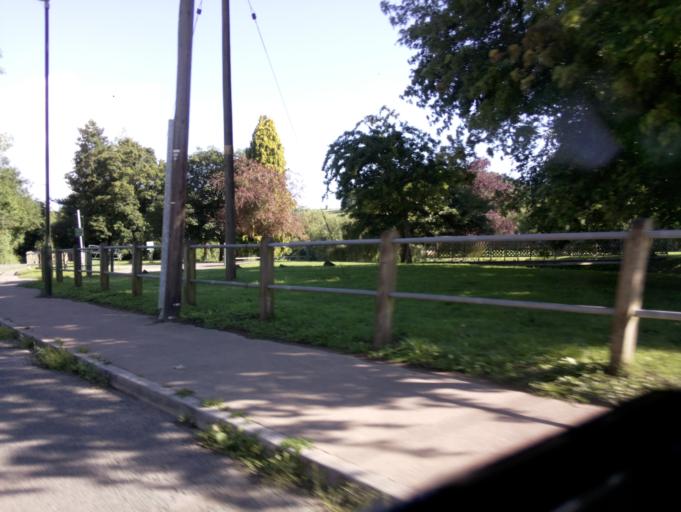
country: GB
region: England
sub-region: Gloucestershire
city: Lydbrook
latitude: 51.8499
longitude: -2.5882
